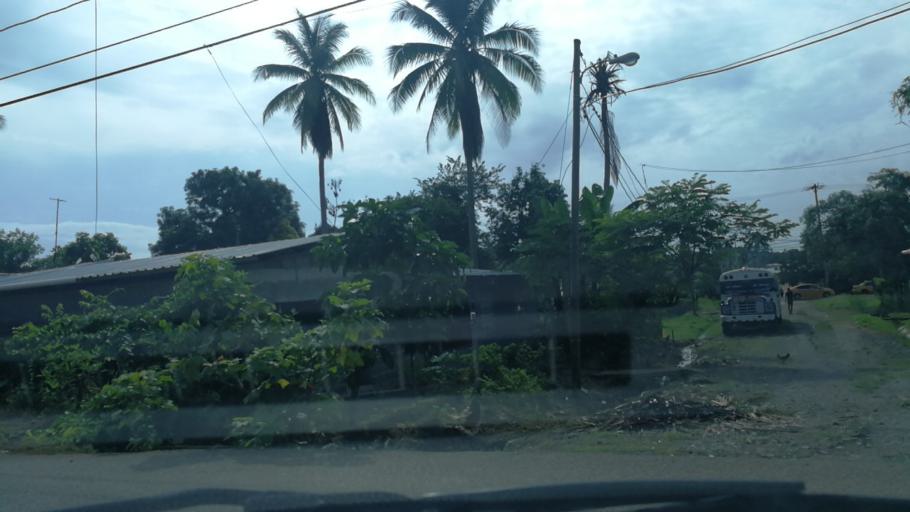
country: PA
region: Panama
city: Pacora
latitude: 9.0816
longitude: -79.2942
